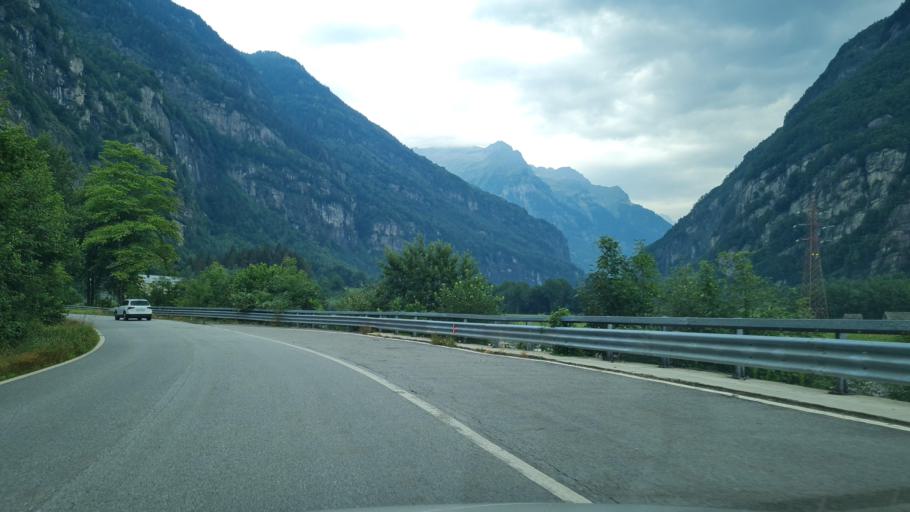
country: IT
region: Piedmont
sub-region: Provincia Verbano-Cusio-Ossola
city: Premia
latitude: 46.2844
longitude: 8.3563
